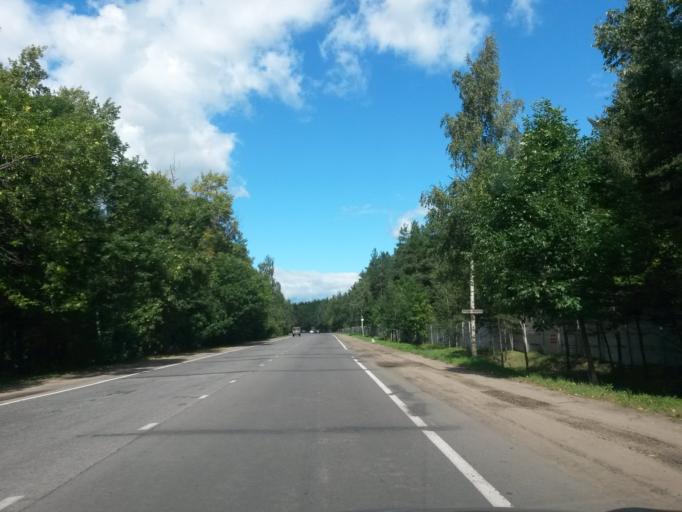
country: RU
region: Jaroslavl
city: Yaroslavl
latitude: 57.6701
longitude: 39.9086
